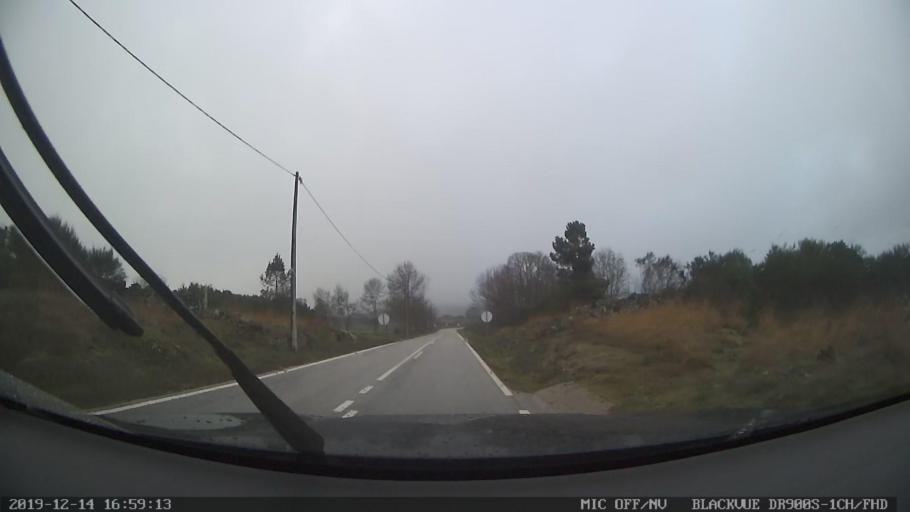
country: PT
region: Vila Real
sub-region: Vila Pouca de Aguiar
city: Vila Pouca de Aguiar
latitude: 41.4350
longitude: -7.5604
